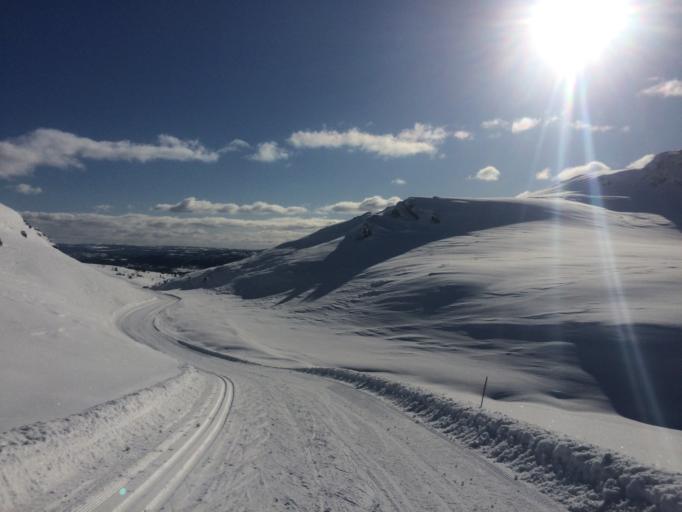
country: NO
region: Oppland
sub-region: Ringebu
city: Ringebu
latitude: 61.3782
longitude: 10.0595
